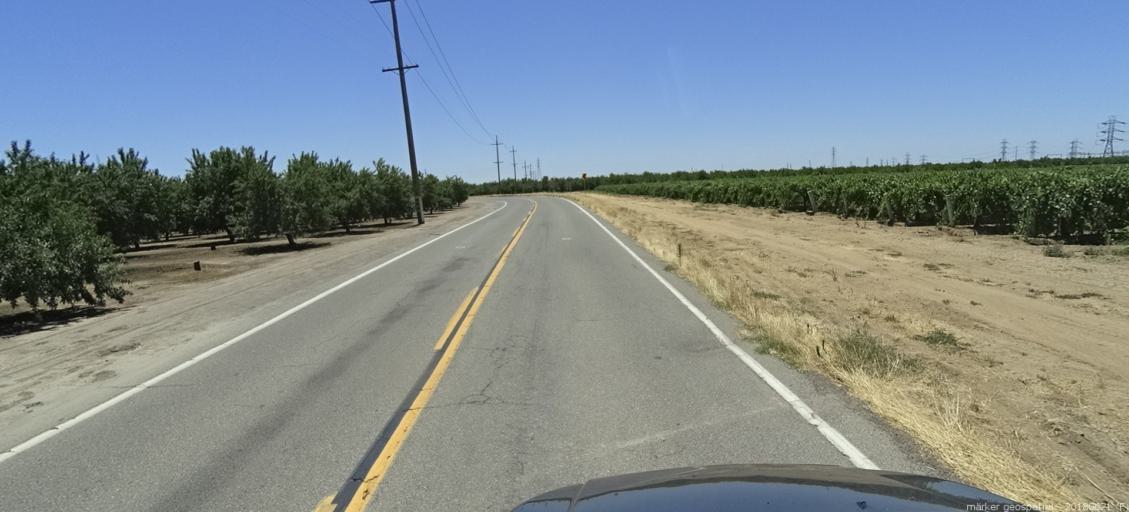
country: US
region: California
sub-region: Fresno County
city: Biola
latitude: 36.8570
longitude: -119.9112
